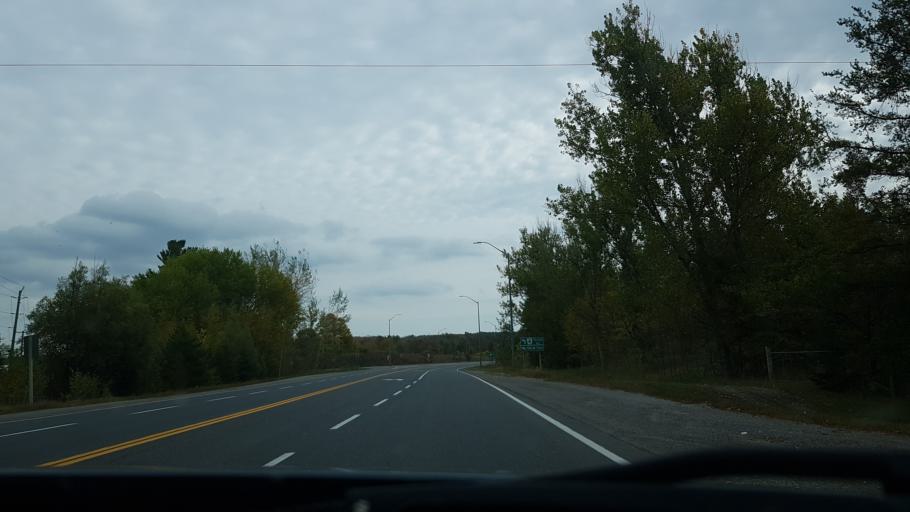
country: CA
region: Ontario
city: Omemee
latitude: 44.5217
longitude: -78.7799
